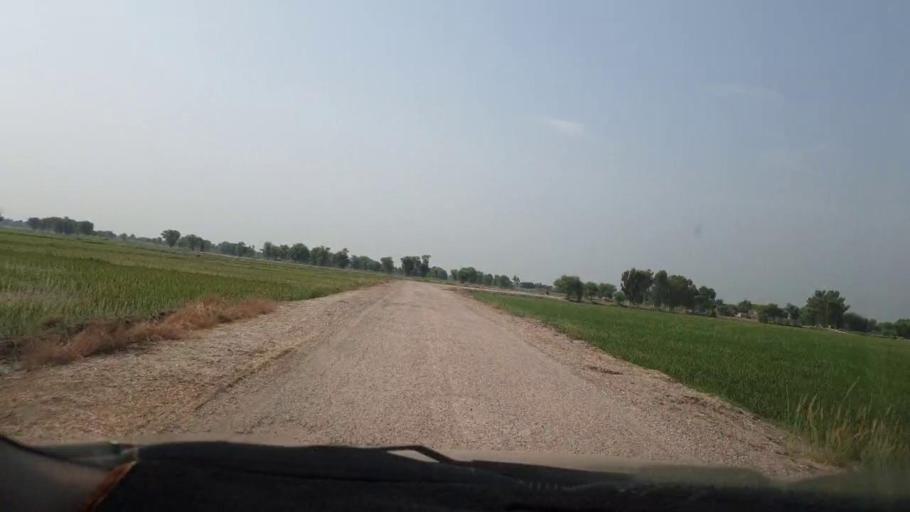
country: PK
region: Sindh
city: Goth Garelo
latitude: 27.4418
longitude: 68.0379
